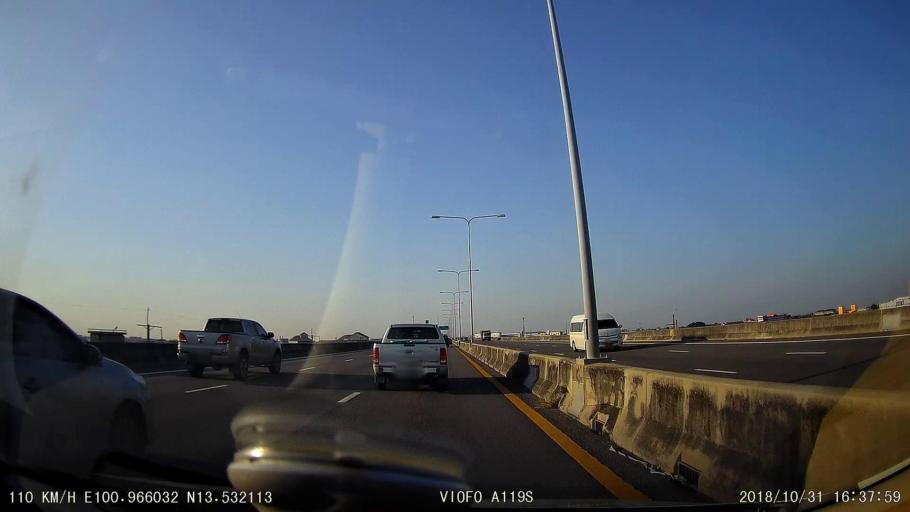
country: TH
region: Chachoengsao
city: Bang Pakong
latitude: 13.5315
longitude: 100.9662
